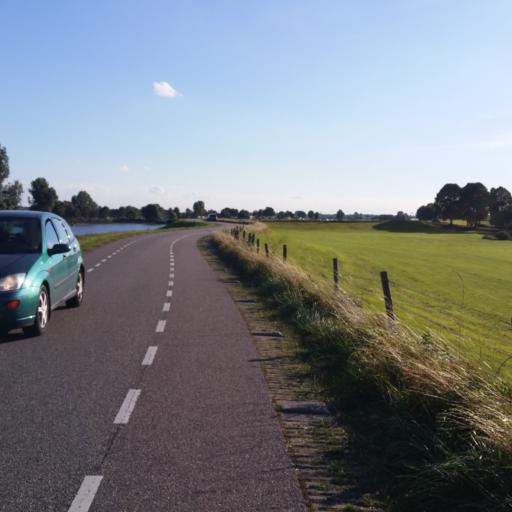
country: NL
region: Utrecht
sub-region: Gemeente Vianen
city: Vianen
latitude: 51.9941
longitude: 5.0627
